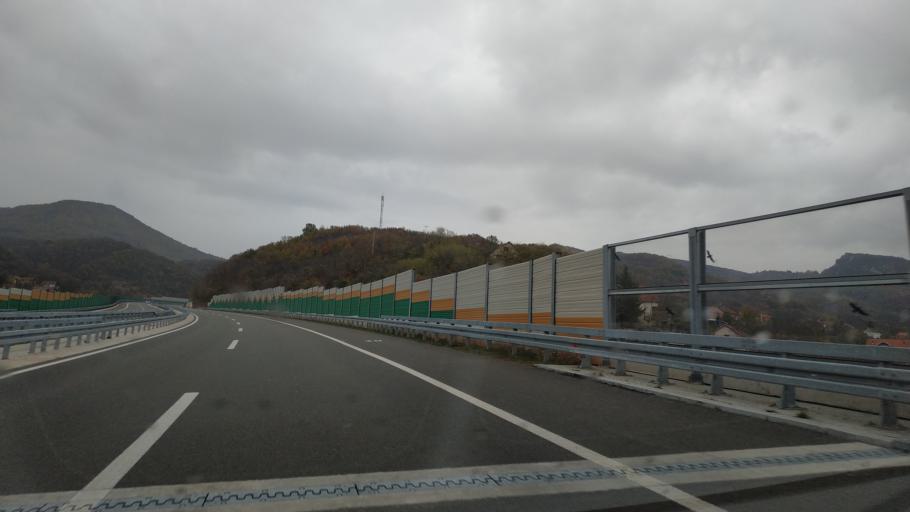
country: RS
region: Central Serbia
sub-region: Nisavski Okrug
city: Niska Banja
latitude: 43.3002
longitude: 22.0506
